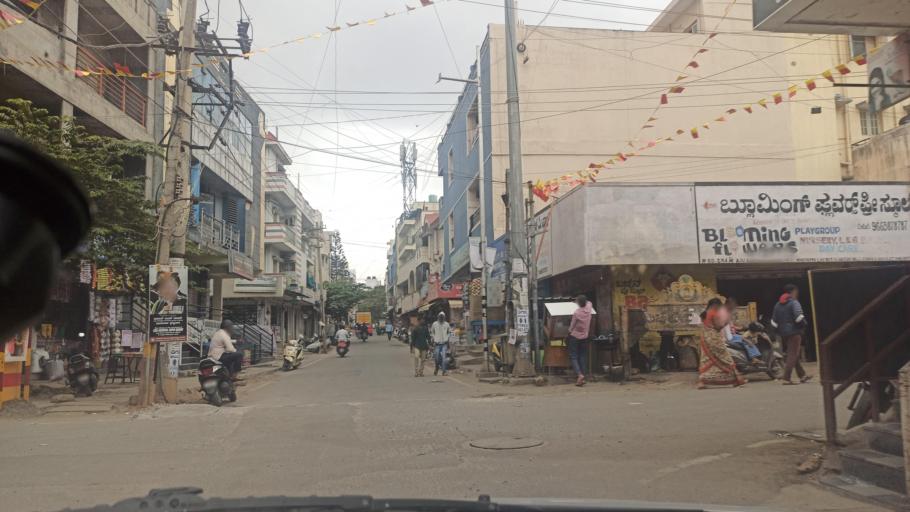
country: IN
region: Karnataka
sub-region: Bangalore Urban
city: Bangalore
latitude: 13.0347
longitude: 77.6044
